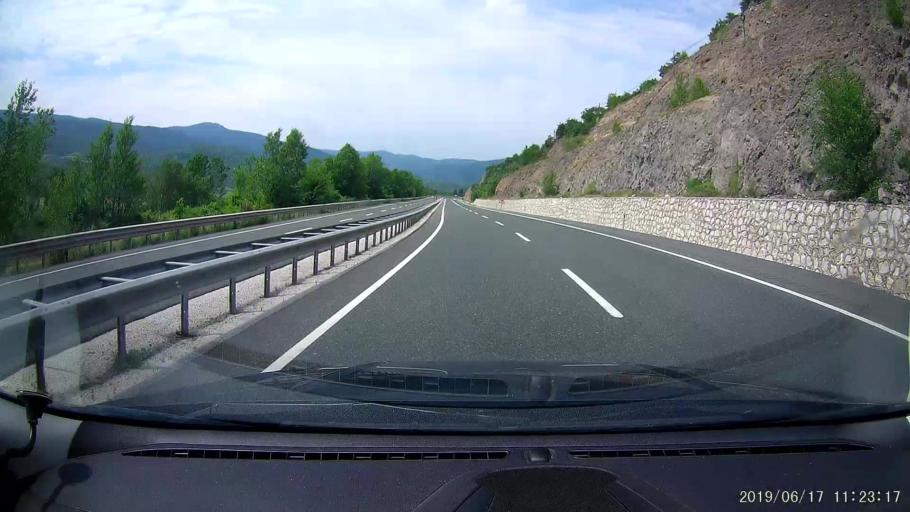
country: TR
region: Cankiri
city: Ilgaz
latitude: 40.8899
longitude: 33.7357
